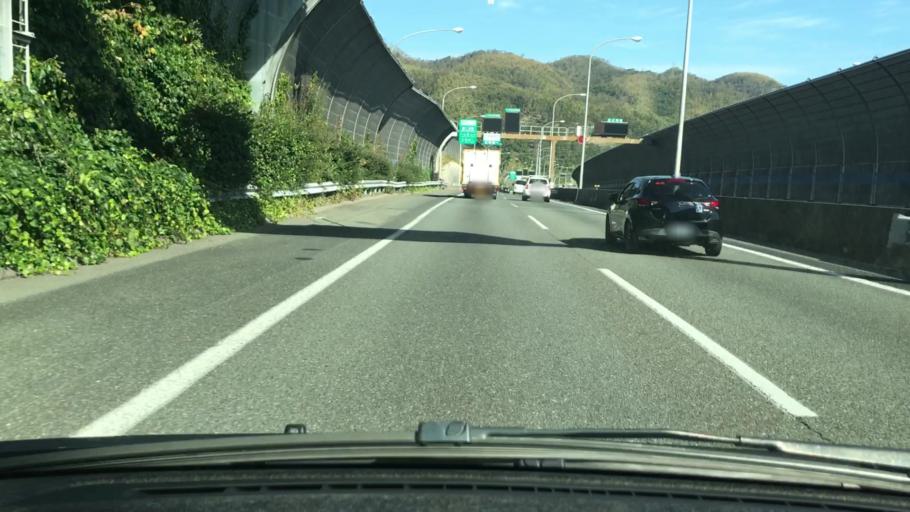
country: JP
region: Kyoto
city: Yawata
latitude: 34.8858
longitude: 135.6610
